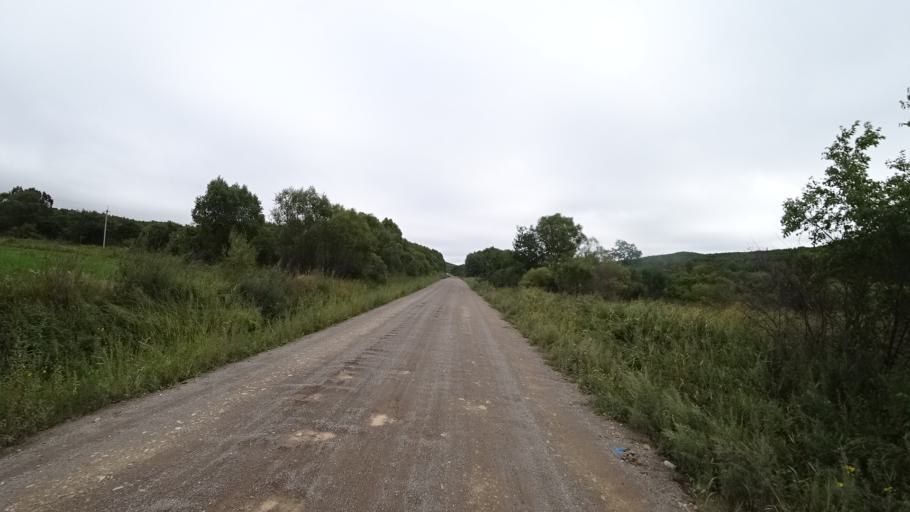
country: RU
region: Primorskiy
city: Ivanovka
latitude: 44.0551
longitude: 132.4808
